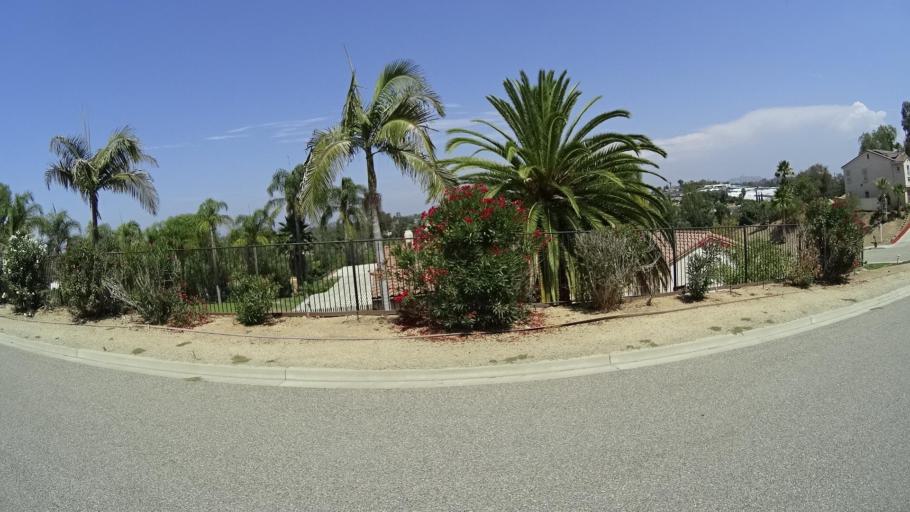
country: US
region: California
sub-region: San Diego County
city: Fallbrook
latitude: 33.3455
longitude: -117.2353
